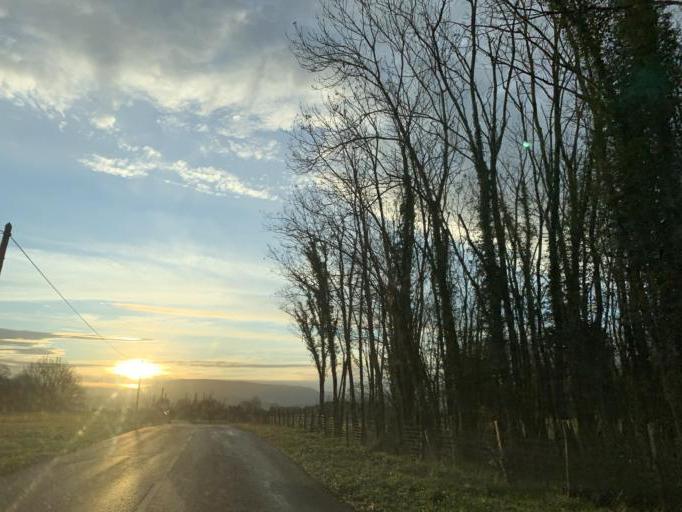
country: FR
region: Rhone-Alpes
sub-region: Departement de l'Ain
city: Virieu-le-Grand
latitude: 45.7970
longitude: 5.6344
